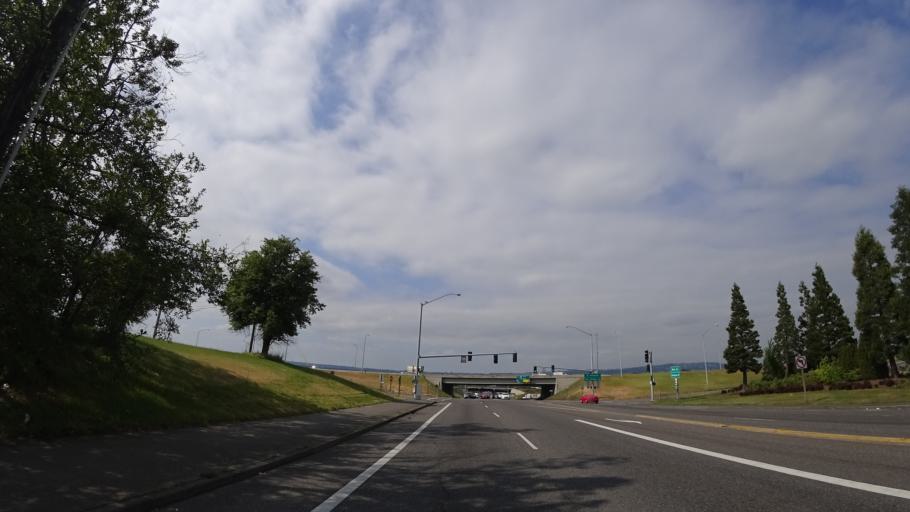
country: US
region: Oregon
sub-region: Multnomah County
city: Fairview
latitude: 45.5401
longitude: -122.4774
